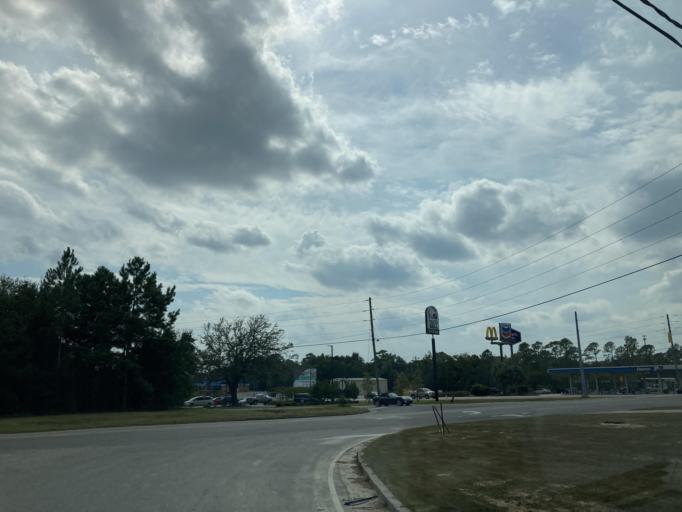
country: US
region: Mississippi
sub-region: Jackson County
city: Gulf Hills
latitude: 30.4506
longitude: -88.8406
